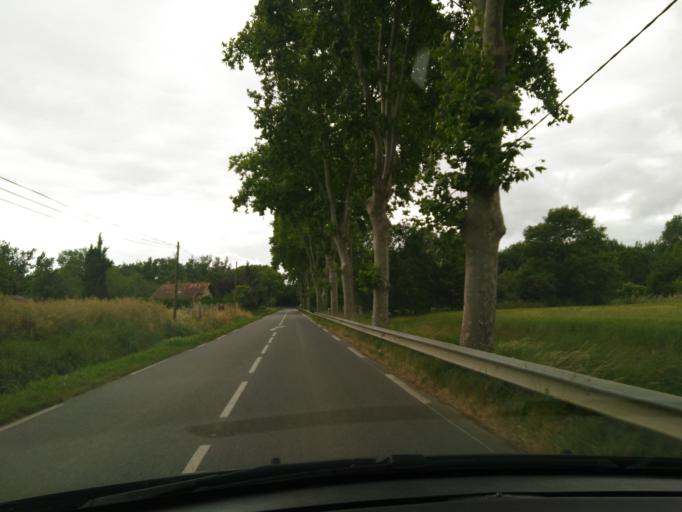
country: FR
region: Midi-Pyrenees
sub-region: Departement de la Haute-Garonne
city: Grenade
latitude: 43.7833
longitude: 1.2808
